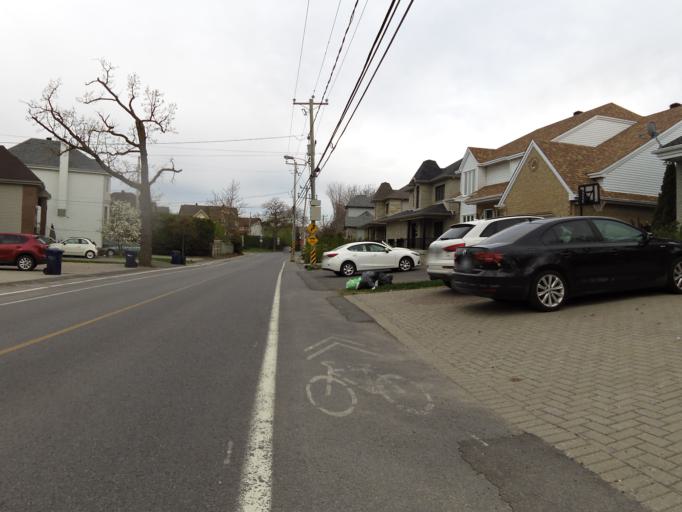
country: CA
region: Quebec
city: Dollard-Des Ormeaux
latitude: 45.5179
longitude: -73.7929
